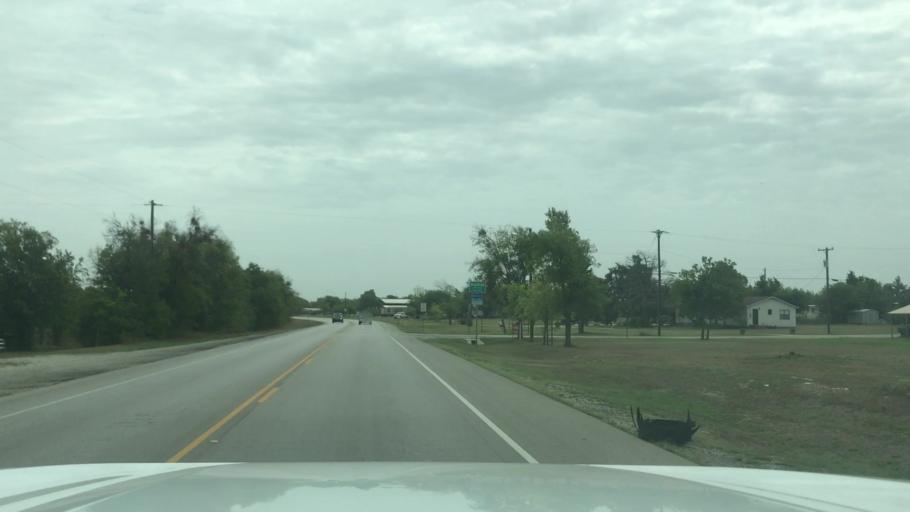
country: US
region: Texas
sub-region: Erath County
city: Dublin
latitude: 32.0897
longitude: -98.3595
